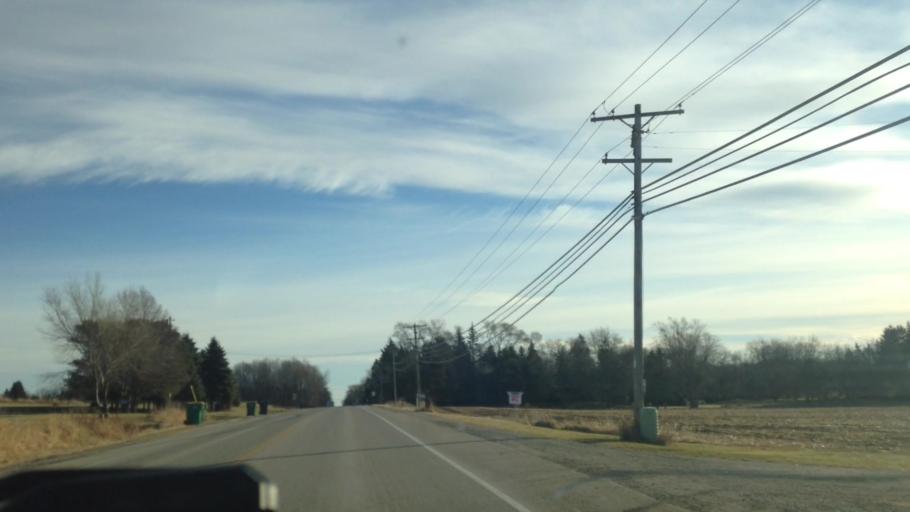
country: US
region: Wisconsin
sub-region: Ozaukee County
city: Cedarburg
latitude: 43.2933
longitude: -88.0315
